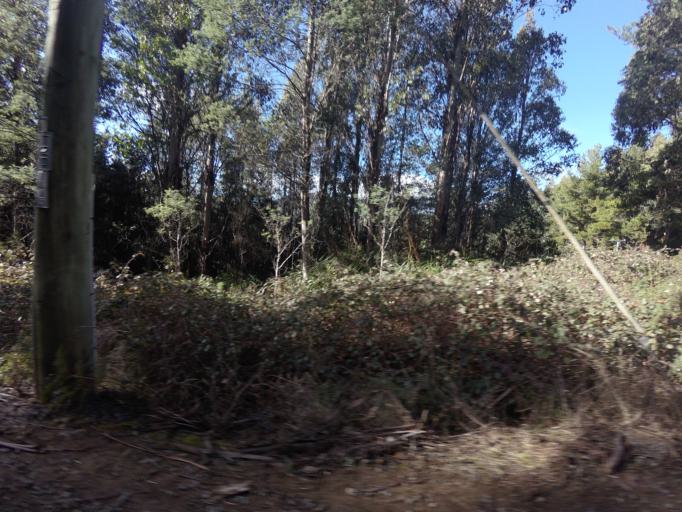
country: AU
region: Tasmania
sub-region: Glenorchy
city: Berriedale
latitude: -42.8541
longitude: 147.1673
